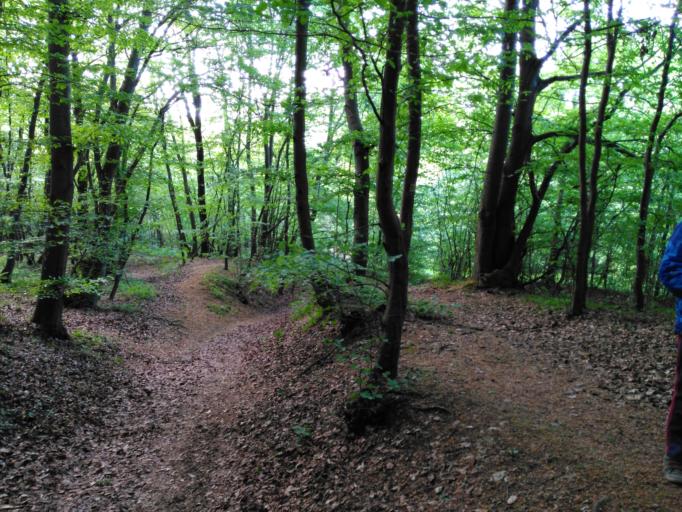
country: CZ
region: Central Bohemia
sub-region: Okres Beroun
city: Kraluv Dvur
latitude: 49.9179
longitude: 14.0668
